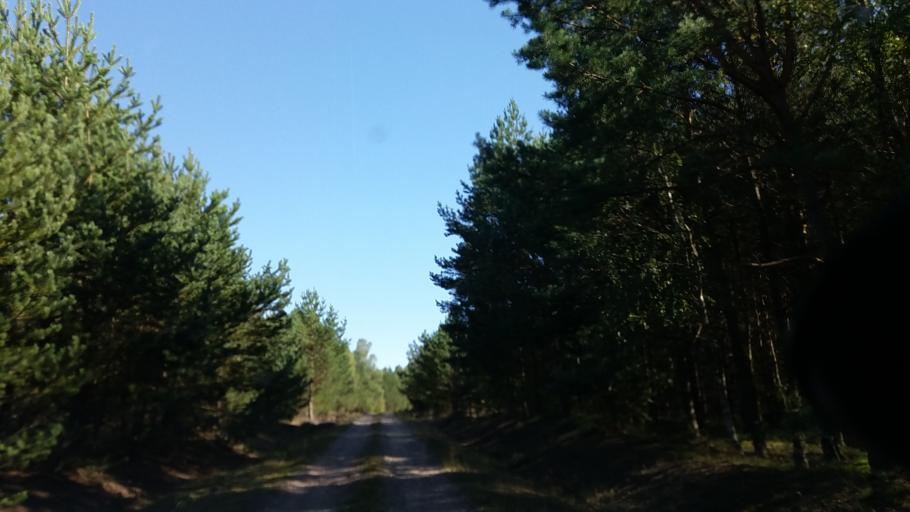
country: PL
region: West Pomeranian Voivodeship
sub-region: Powiat szczecinecki
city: Borne Sulinowo
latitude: 53.5672
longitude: 16.4973
